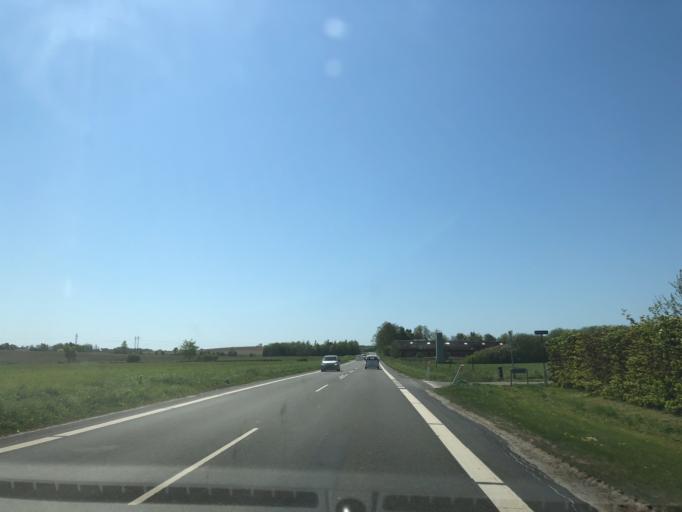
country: DK
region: Zealand
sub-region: Slagelse Kommune
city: Korsor
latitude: 55.3285
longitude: 11.2018
